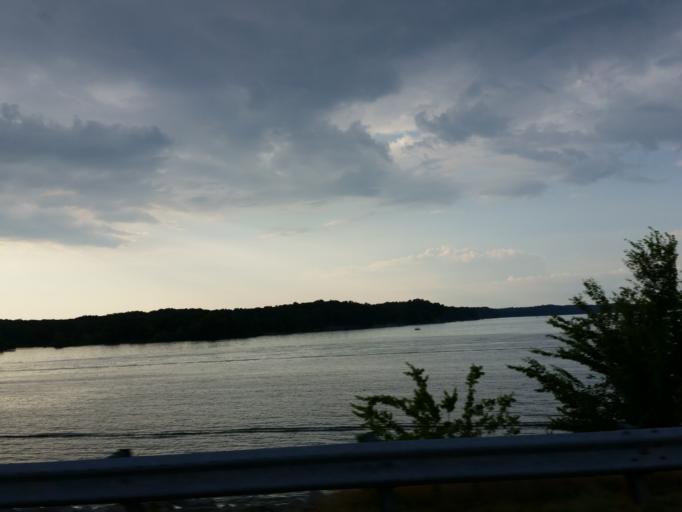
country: US
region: Tennessee
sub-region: Stewart County
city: Dover
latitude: 36.4411
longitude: -88.0741
